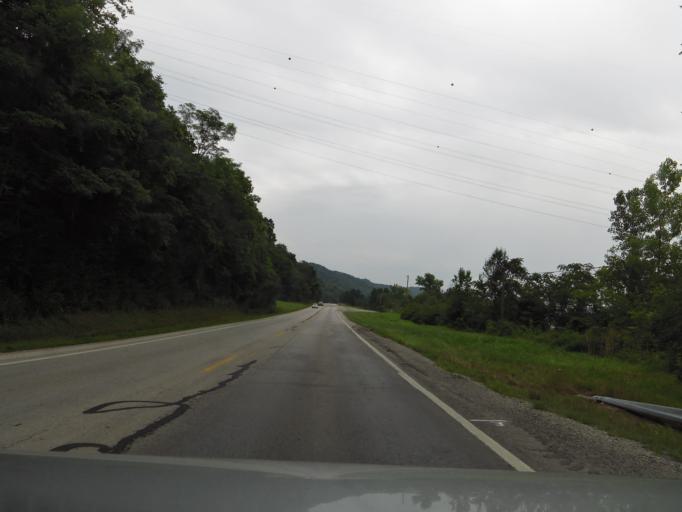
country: US
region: Ohio
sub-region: Brown County
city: Aberdeen
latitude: 38.7036
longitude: -83.7925
